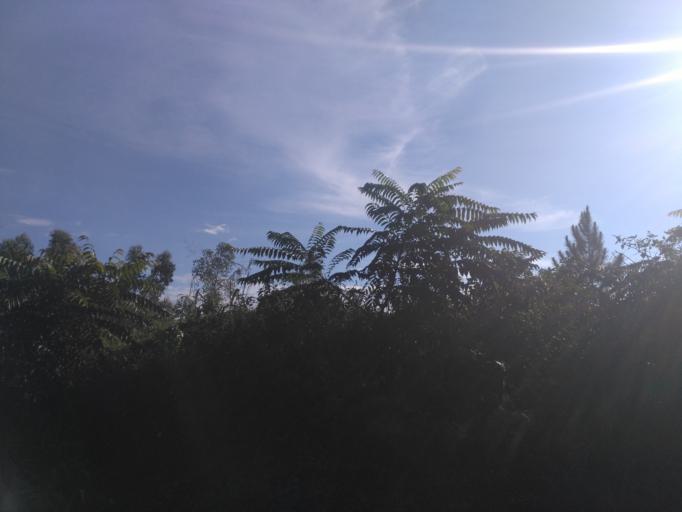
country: UG
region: Eastern Region
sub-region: Jinja District
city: Jinja
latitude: 0.4616
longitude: 33.1828
